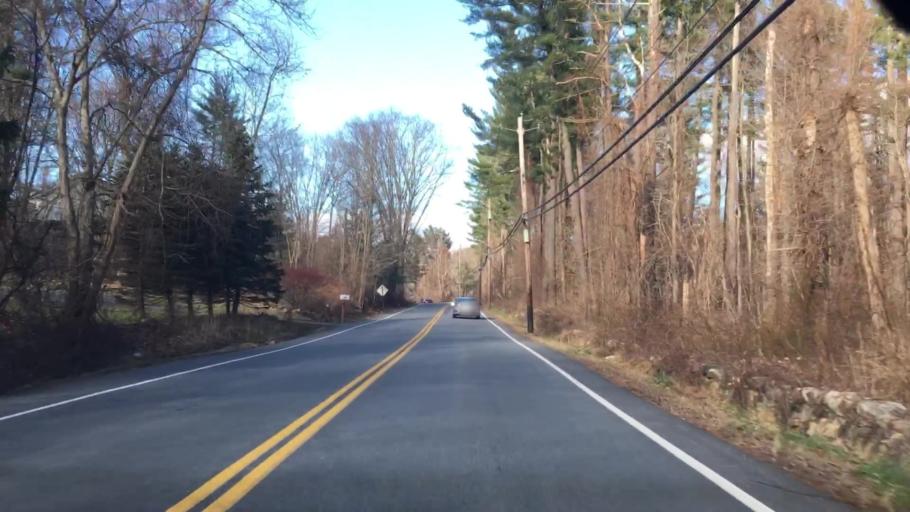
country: US
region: New York
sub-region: Putnam County
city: Carmel Hamlet
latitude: 41.4047
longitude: -73.6633
